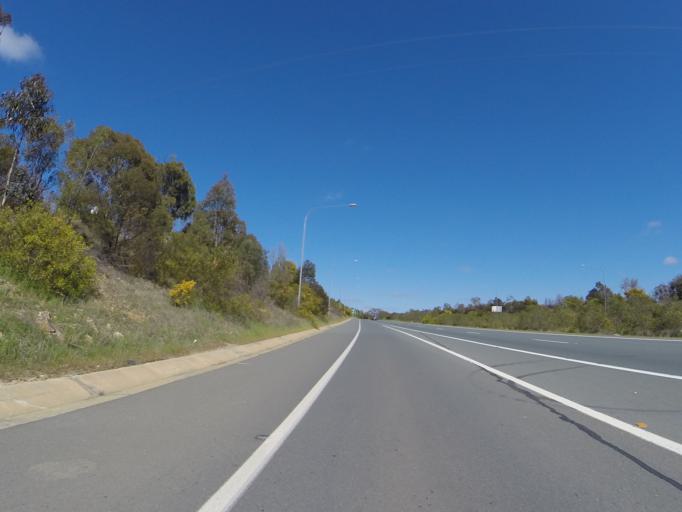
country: AU
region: Australian Capital Territory
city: Kaleen
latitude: -35.2034
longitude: 149.2077
